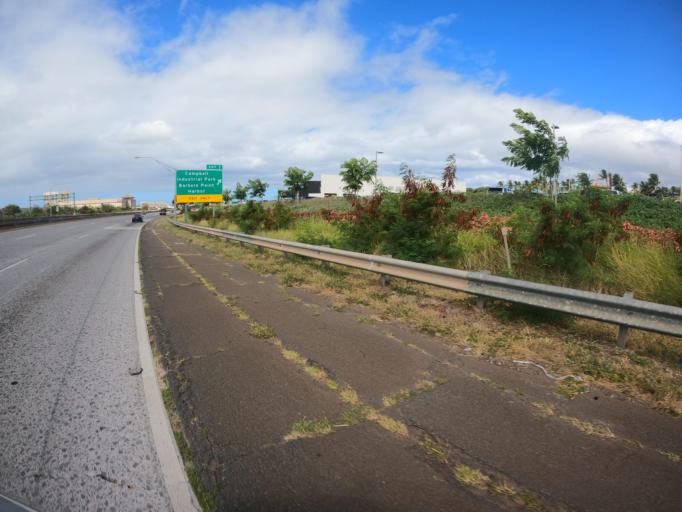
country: US
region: Hawaii
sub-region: Honolulu County
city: Makakilo City
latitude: 21.3341
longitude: -158.0851
